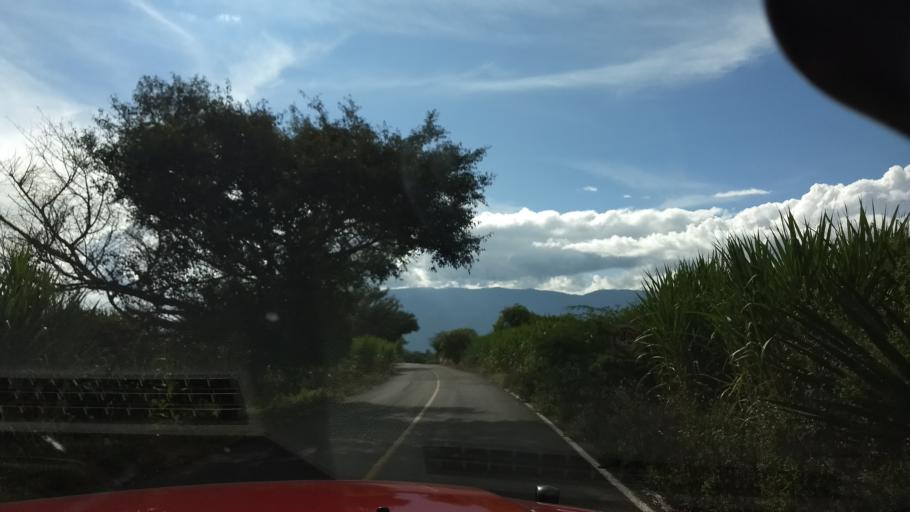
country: MX
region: Colima
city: Suchitlan
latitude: 19.4674
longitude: -103.7575
